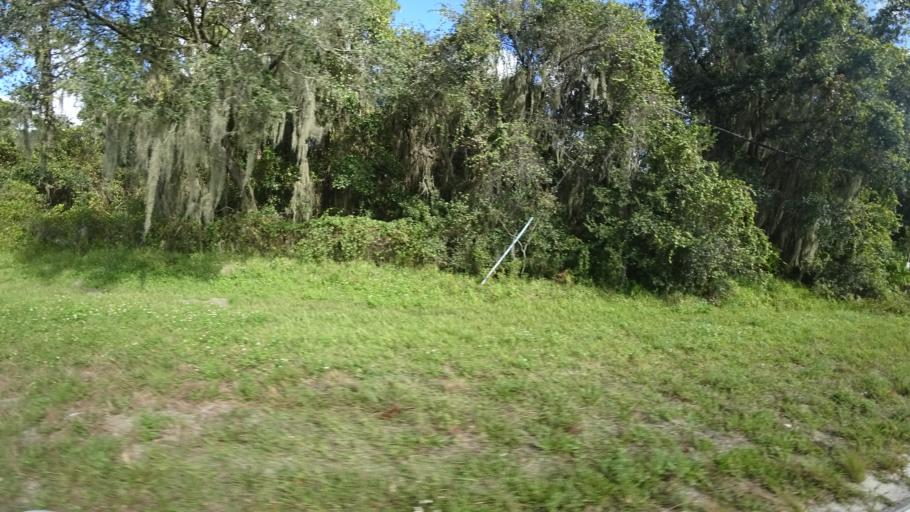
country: US
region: Florida
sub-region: Sarasota County
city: Lake Sarasota
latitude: 27.3464
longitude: -82.2412
